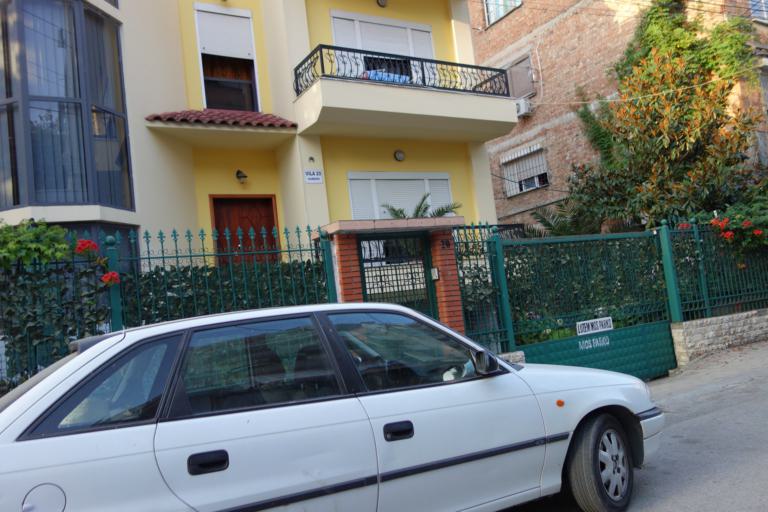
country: AL
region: Tirane
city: Tirana
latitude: 41.3243
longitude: 19.8096
